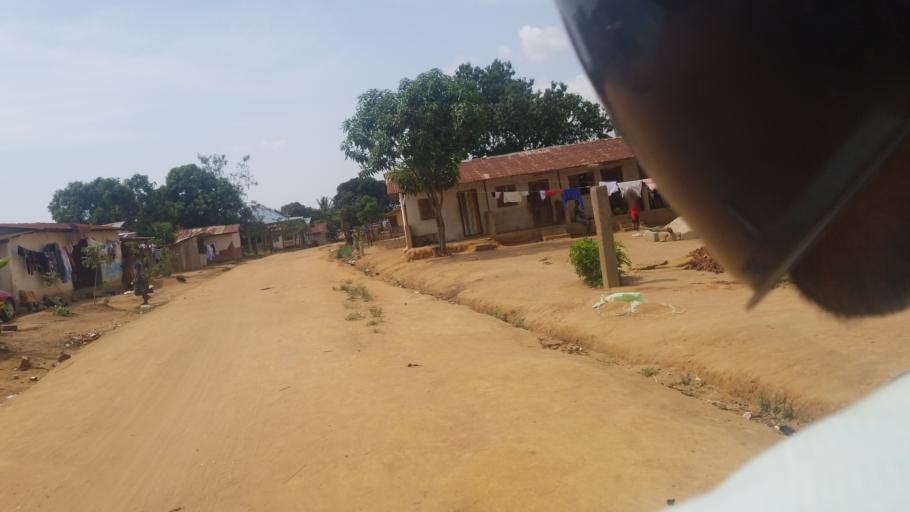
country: SL
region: Western Area
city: Waterloo
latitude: 8.3178
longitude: -13.0446
